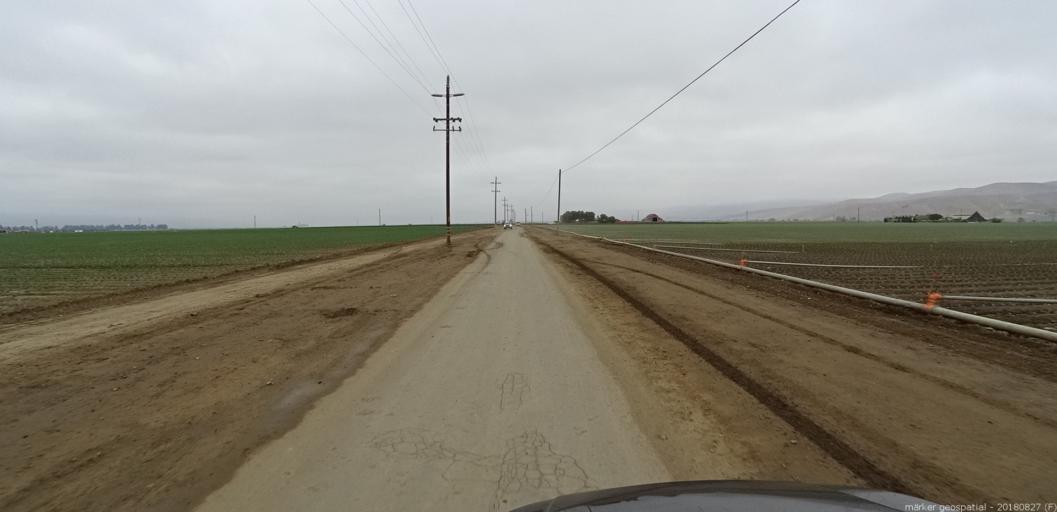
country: US
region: California
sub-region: Monterey County
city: Greenfield
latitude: 36.3395
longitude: -121.2348
